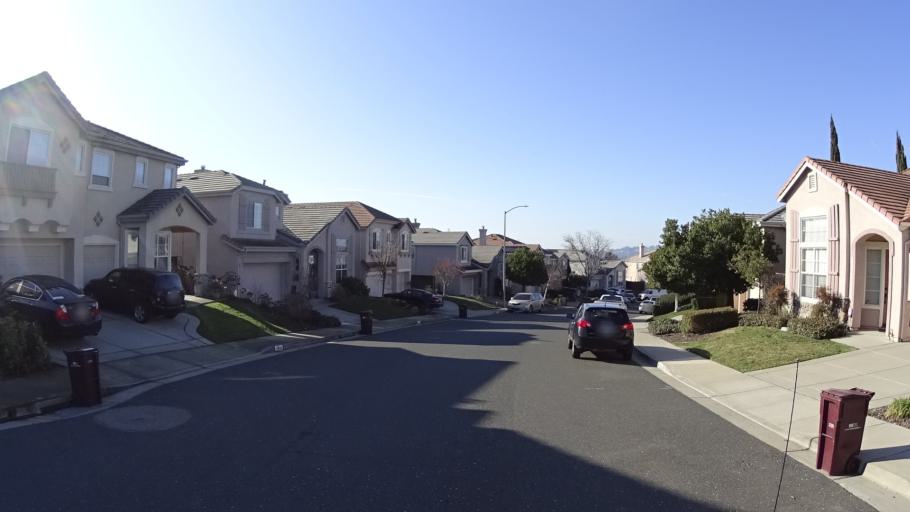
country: US
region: California
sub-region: Alameda County
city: Fairview
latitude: 37.6911
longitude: -122.0451
